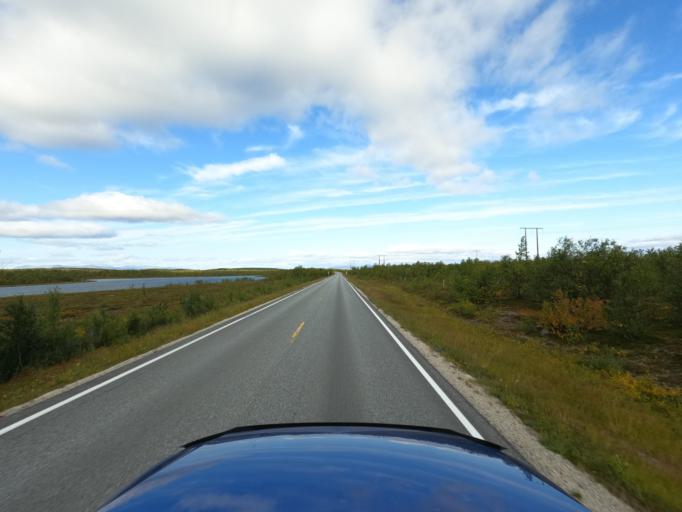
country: NO
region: Finnmark Fylke
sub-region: Karasjok
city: Karasjohka
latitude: 69.6603
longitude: 25.2769
